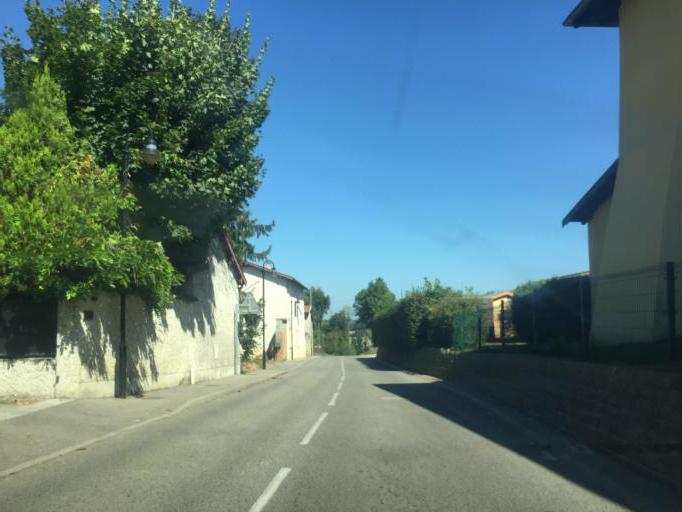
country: FR
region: Rhone-Alpes
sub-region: Departement de l'Ain
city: Tramoyes
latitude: 45.8779
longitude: 4.9686
